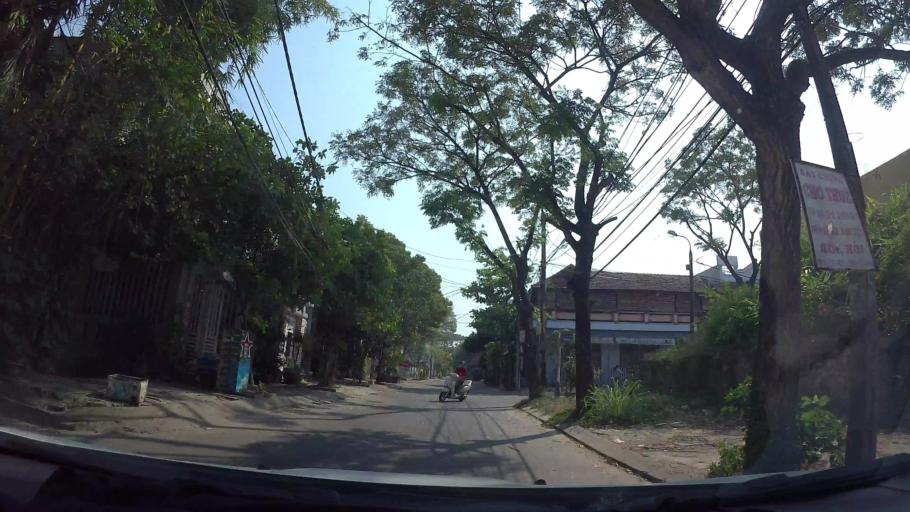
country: VN
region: Da Nang
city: Cam Le
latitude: 16.0091
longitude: 108.1936
